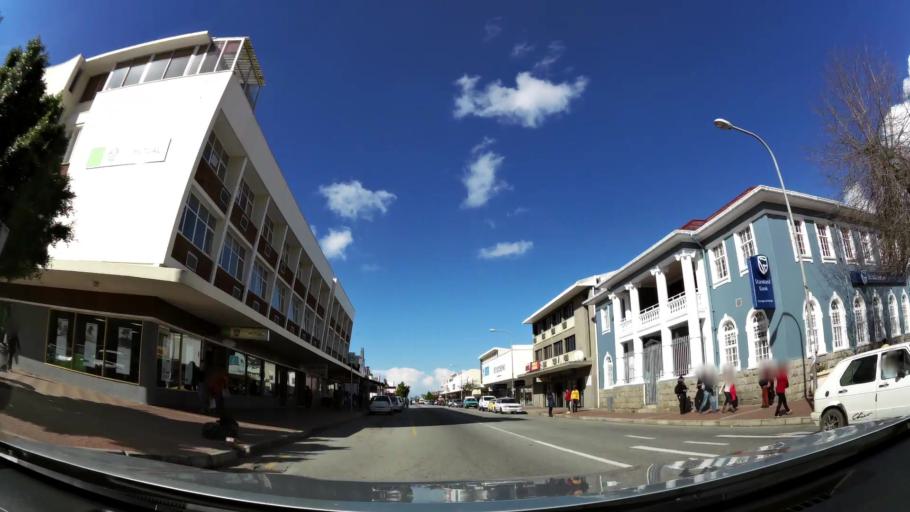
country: ZA
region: Western Cape
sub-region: Eden District Municipality
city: George
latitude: -33.9589
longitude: 22.4571
